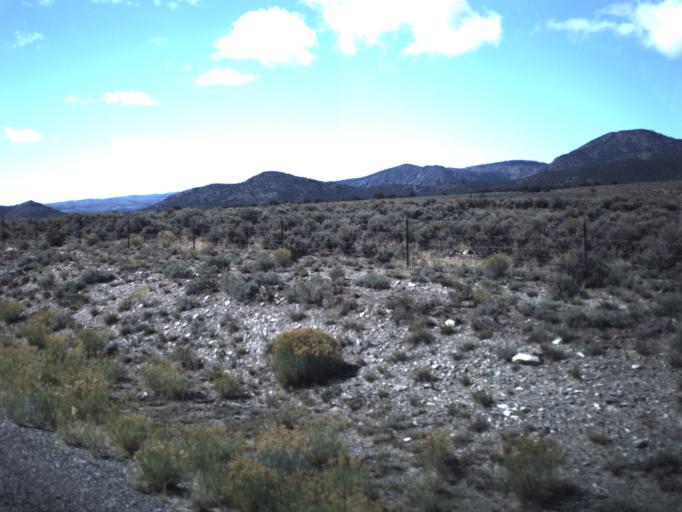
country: US
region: Utah
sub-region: Piute County
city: Junction
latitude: 38.3380
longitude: -111.9541
